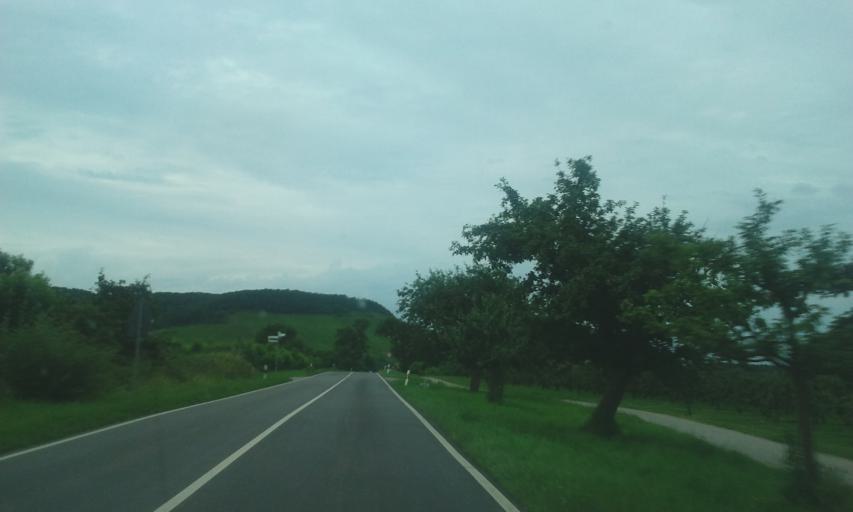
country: DE
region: Baden-Wuerttemberg
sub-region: Karlsruhe Region
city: Illingen
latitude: 48.9646
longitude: 8.9428
